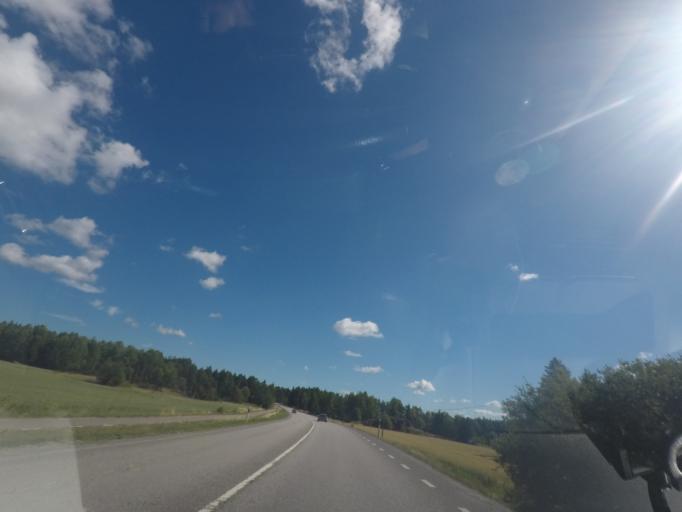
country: SE
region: Uppsala
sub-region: Uppsala Kommun
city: Saevja
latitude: 59.8490
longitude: 17.7805
